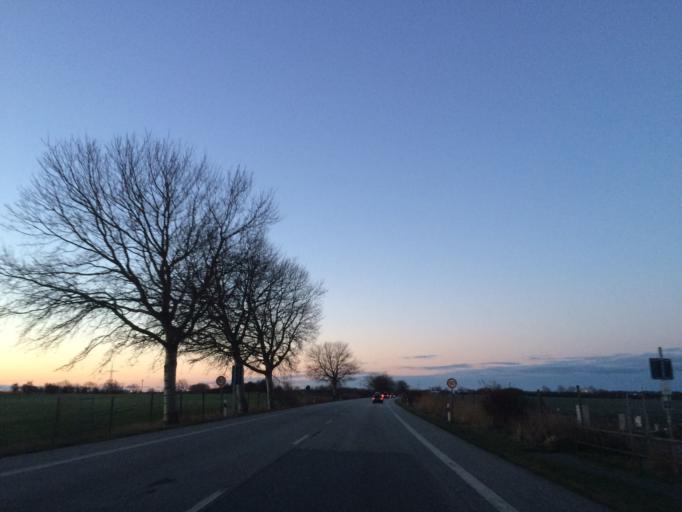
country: DE
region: Schleswig-Holstein
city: Grossenbrode
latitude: 54.3882
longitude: 11.1024
